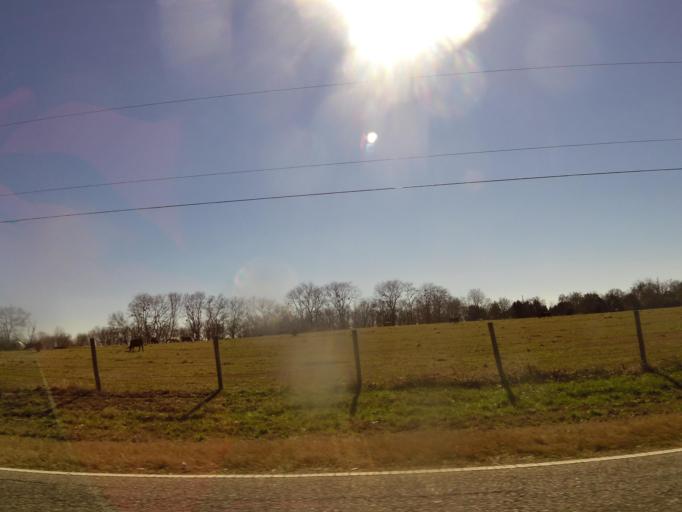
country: US
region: Alabama
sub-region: Montgomery County
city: Pike Road
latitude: 32.2833
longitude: -86.0948
